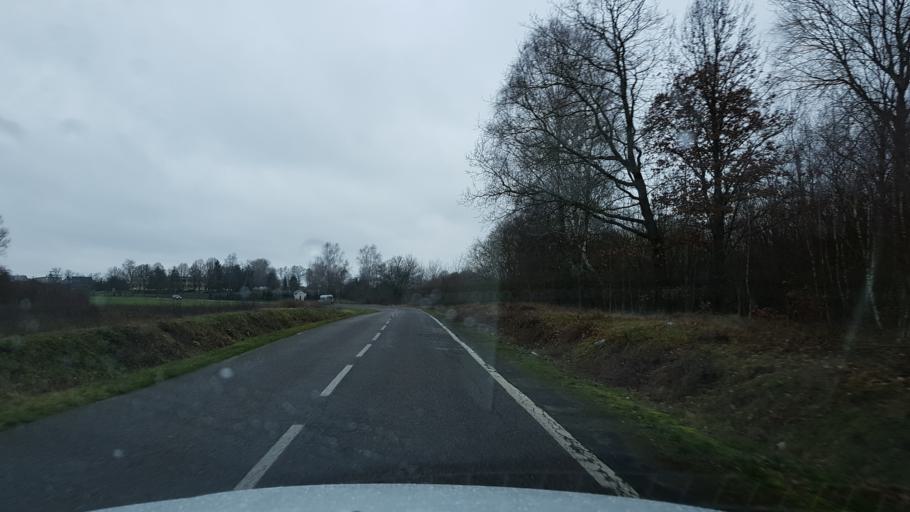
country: PL
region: West Pomeranian Voivodeship
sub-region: Powiat lobeski
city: Radowo Male
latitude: 53.6200
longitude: 15.4858
